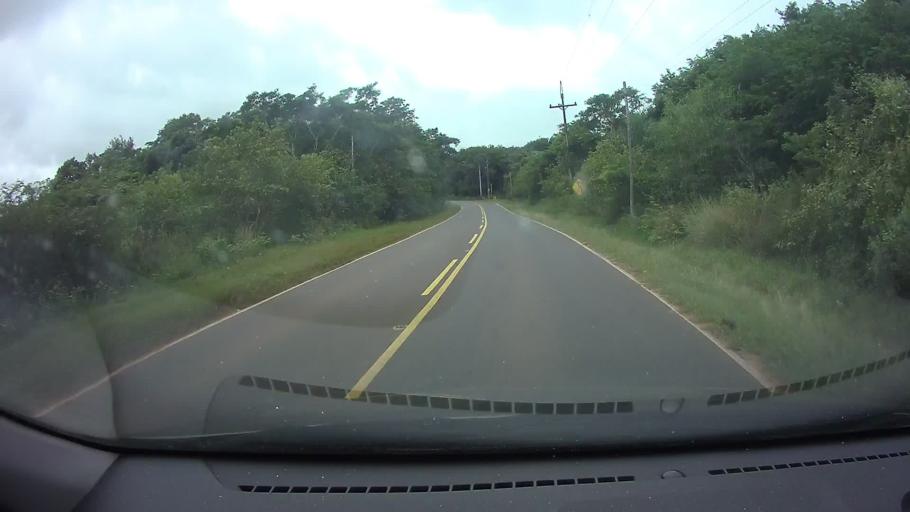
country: PY
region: Central
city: Nueva Italia
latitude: -25.6122
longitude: -57.4355
